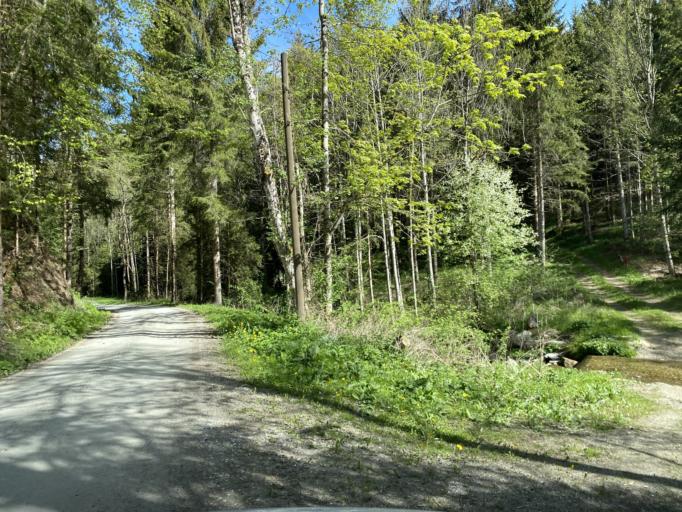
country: AT
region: Styria
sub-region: Politischer Bezirk Weiz
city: Gschaid bei Birkfeld
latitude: 47.3412
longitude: 15.7115
